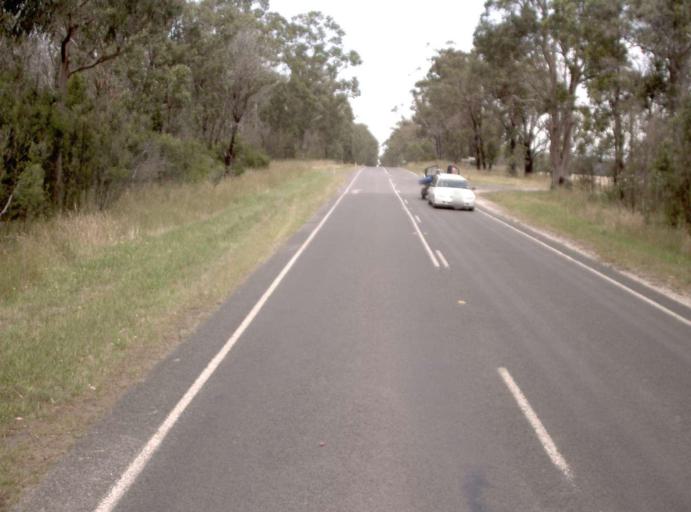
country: AU
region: Victoria
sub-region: Latrobe
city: Traralgon
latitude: -38.5142
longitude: 146.7082
